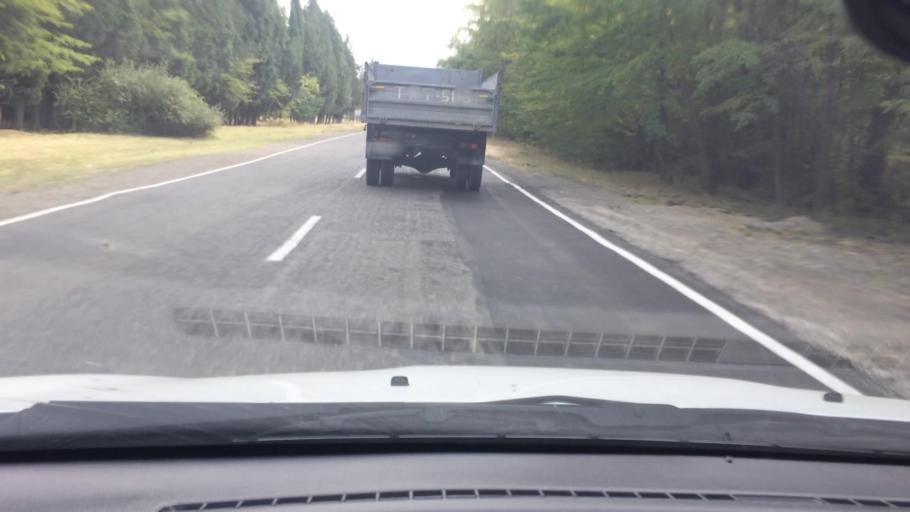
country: GE
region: Kvemo Kartli
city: Rust'avi
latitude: 41.4666
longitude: 44.9822
